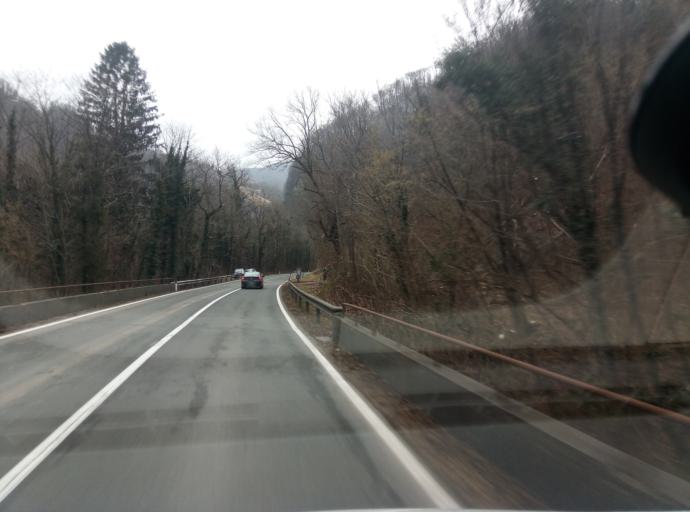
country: SI
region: Zagorje ob Savi
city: Kisovec
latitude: 46.0993
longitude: 14.9589
